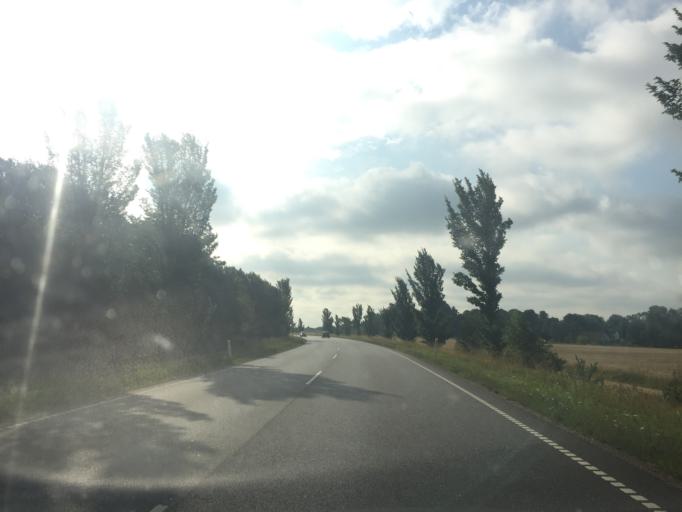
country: DK
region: Capital Region
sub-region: Hillerod Kommune
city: Hillerod
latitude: 55.9376
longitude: 12.2238
